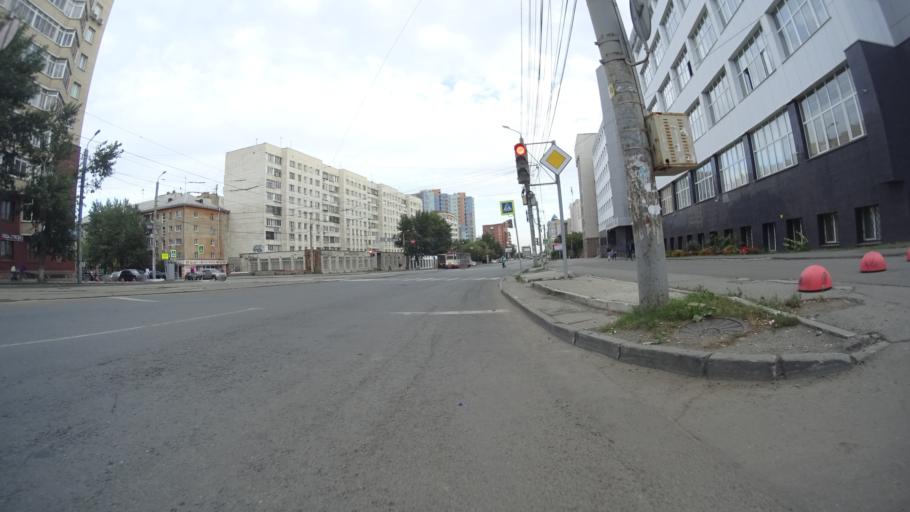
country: RU
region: Chelyabinsk
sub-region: Gorod Chelyabinsk
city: Chelyabinsk
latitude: 55.1502
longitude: 61.4113
